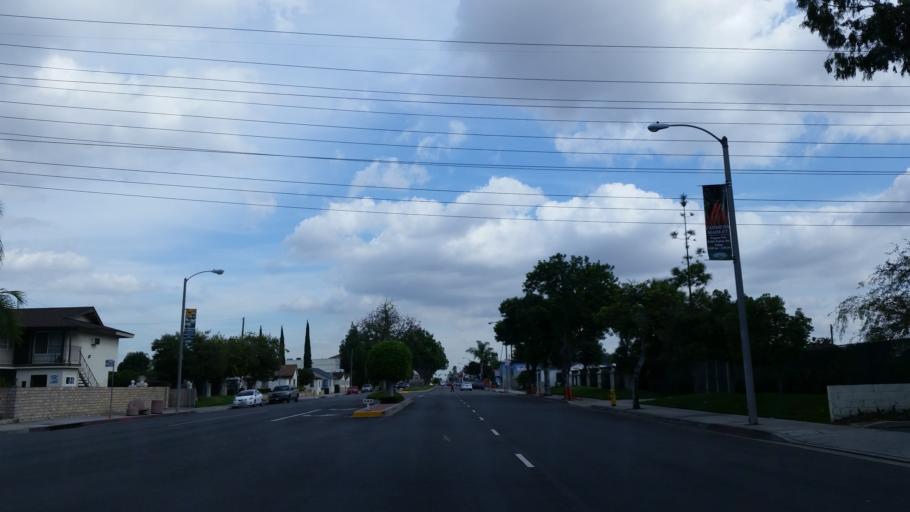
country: US
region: California
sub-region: Los Angeles County
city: Paramount
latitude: 33.8892
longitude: -118.1482
